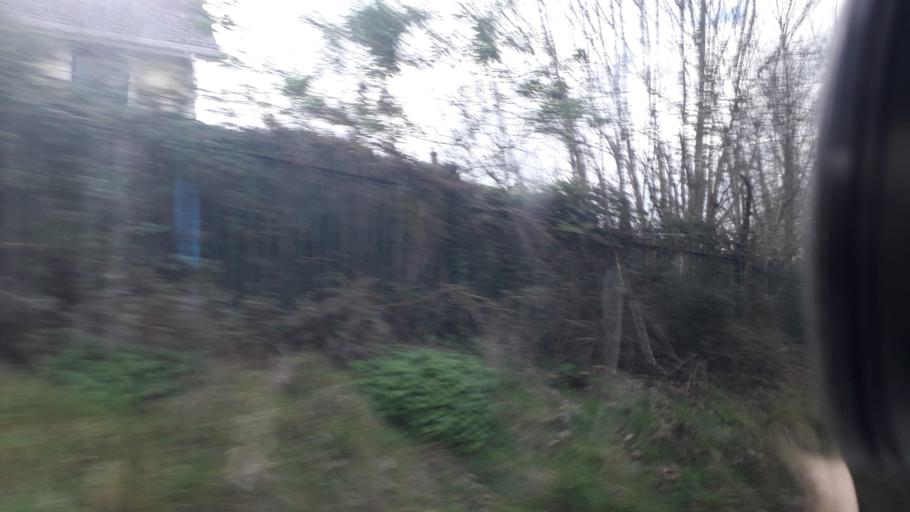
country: IE
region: Leinster
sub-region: An Iarmhi
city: An Muileann gCearr
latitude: 53.5178
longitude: -7.3314
